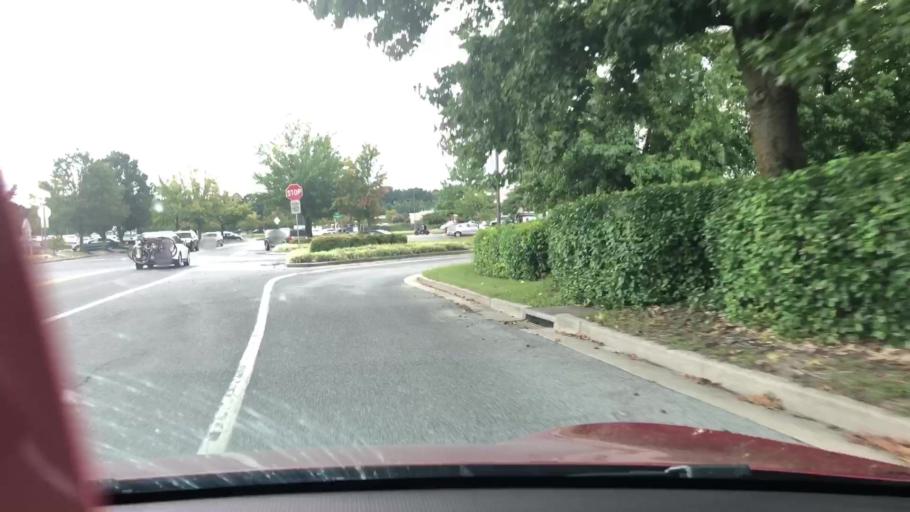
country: US
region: Maryland
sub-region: Wicomico County
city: Salisbury
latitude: 38.4016
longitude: -75.5683
